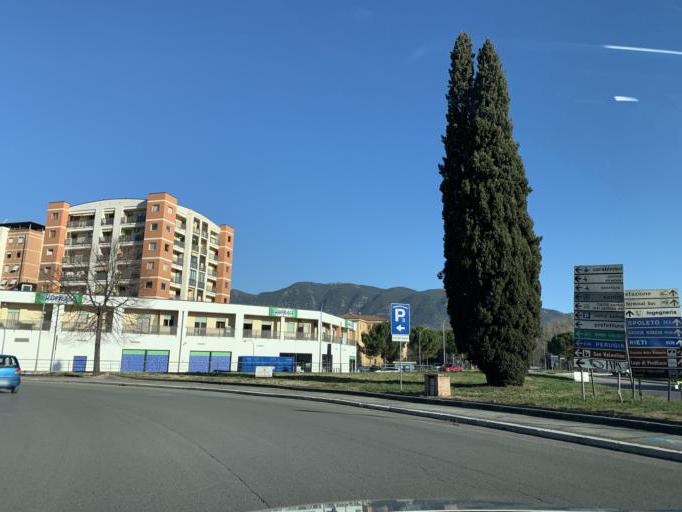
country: IT
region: Umbria
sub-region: Provincia di Terni
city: Terni
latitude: 42.5591
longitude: 12.6570
